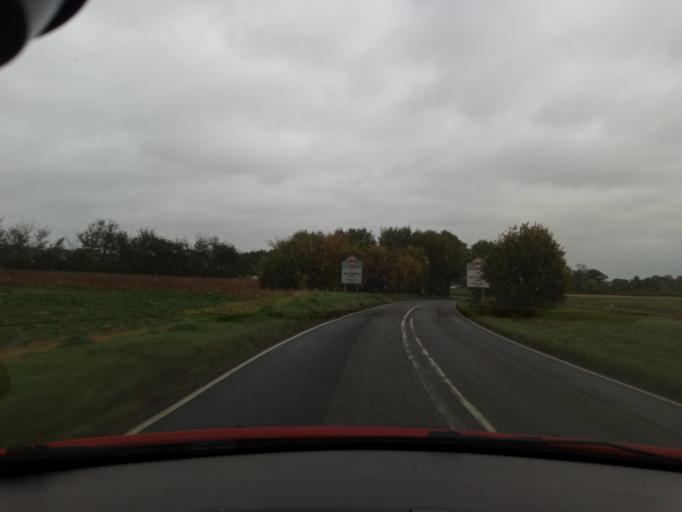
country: GB
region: England
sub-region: Suffolk
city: Kedington
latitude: 52.0529
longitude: 0.5119
